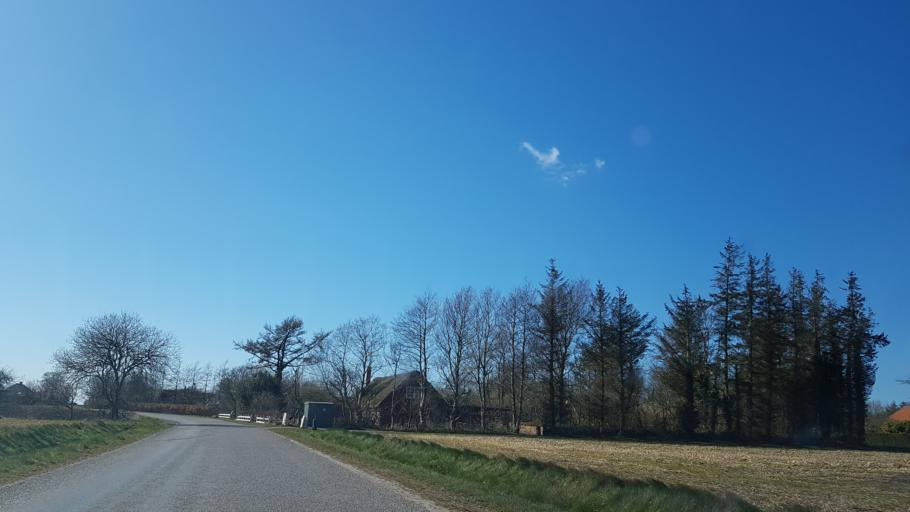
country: DK
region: South Denmark
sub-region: Esbjerg Kommune
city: Ribe
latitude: 55.2525
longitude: 8.7025
